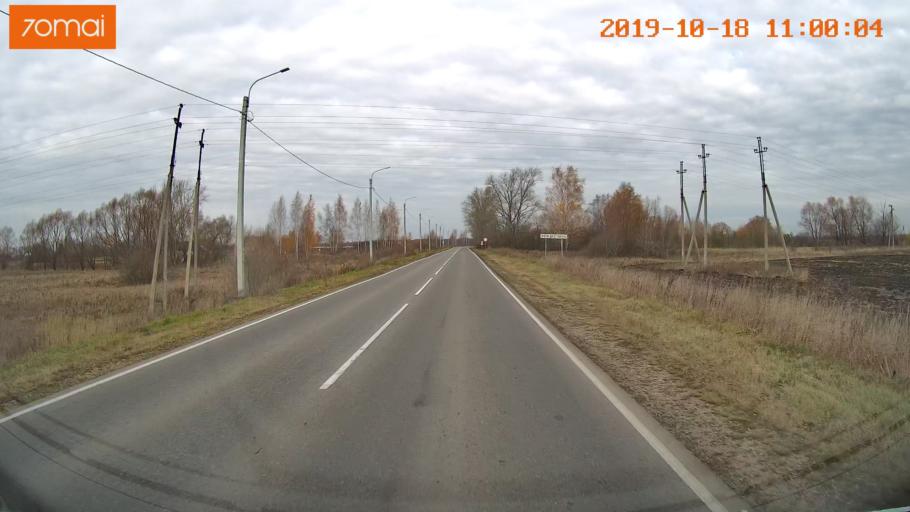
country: RU
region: Tula
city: Yepifan'
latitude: 53.8385
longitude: 38.5538
